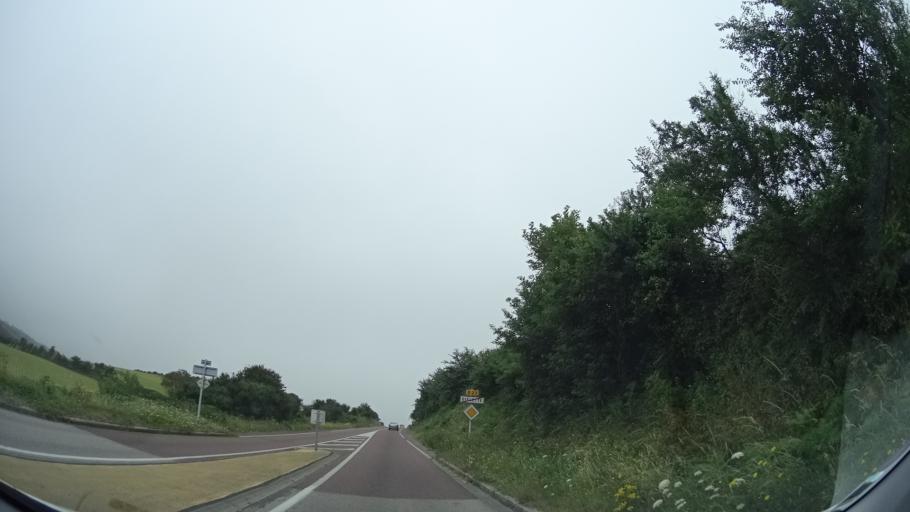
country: FR
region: Lower Normandy
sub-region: Departement de la Manche
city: Flamanville
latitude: 49.5499
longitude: -1.8560
